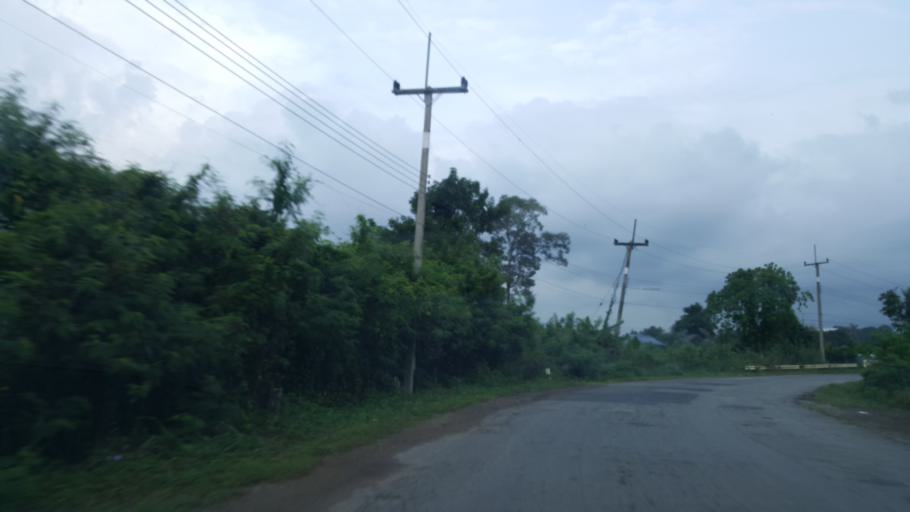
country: TH
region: Chon Buri
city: Sattahip
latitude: 12.7261
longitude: 100.9138
